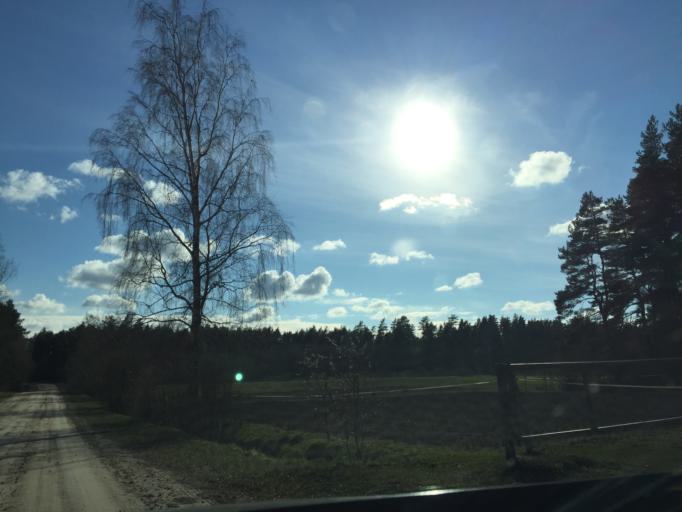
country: LV
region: Kekava
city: Kekava
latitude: 56.8511
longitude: 24.1855
